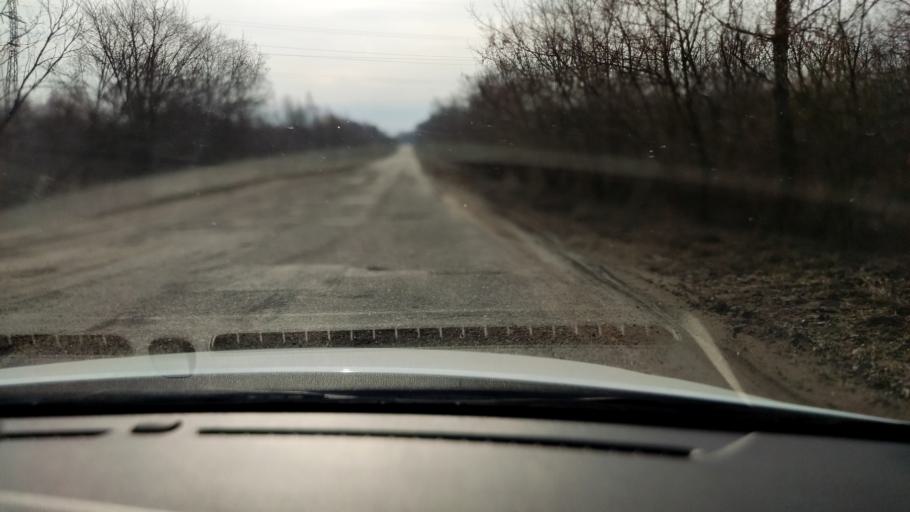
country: RU
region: Tatarstan
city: Stolbishchi
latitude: 55.7196
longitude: 49.2133
